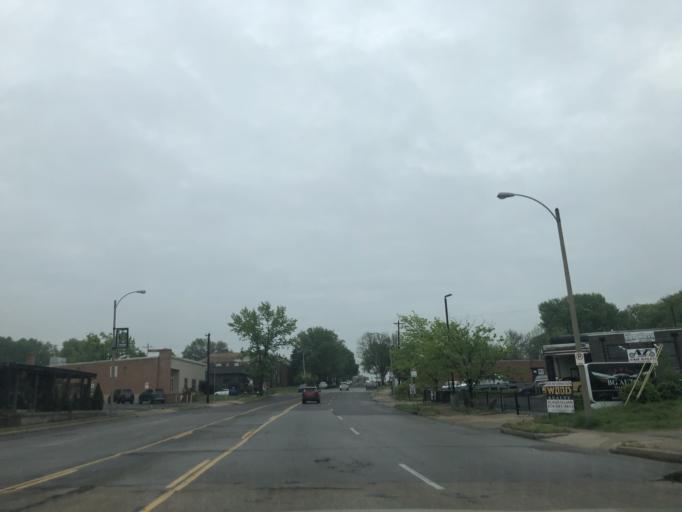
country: US
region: Missouri
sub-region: Saint Louis County
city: Shrewsbury
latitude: 38.5870
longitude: -90.3130
